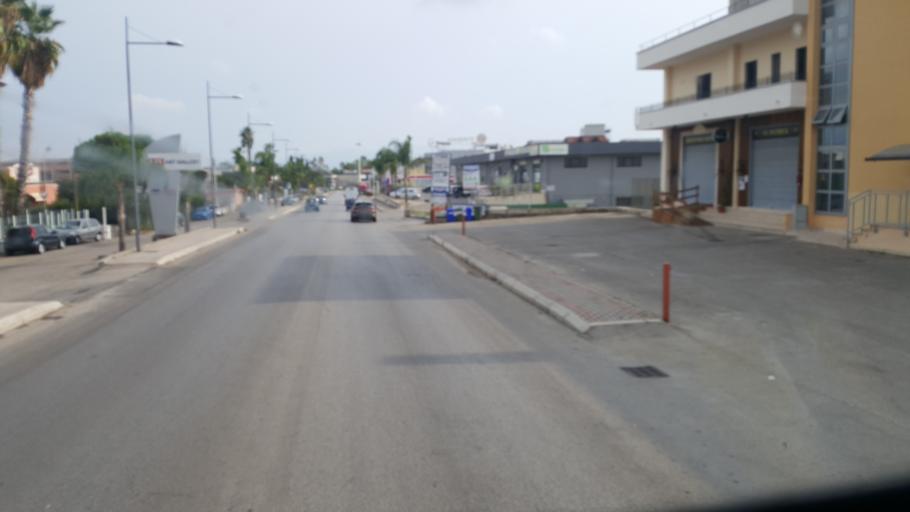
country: IT
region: Campania
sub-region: Provincia di Salerno
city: Battipaglia
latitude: 40.5991
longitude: 14.9868
